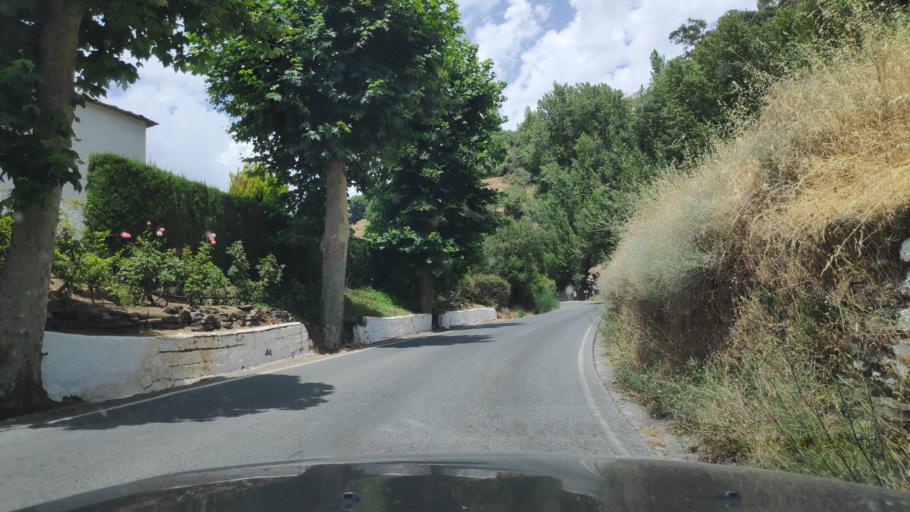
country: ES
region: Andalusia
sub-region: Provincia de Granada
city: Bubion
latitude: 36.9542
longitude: -3.3553
